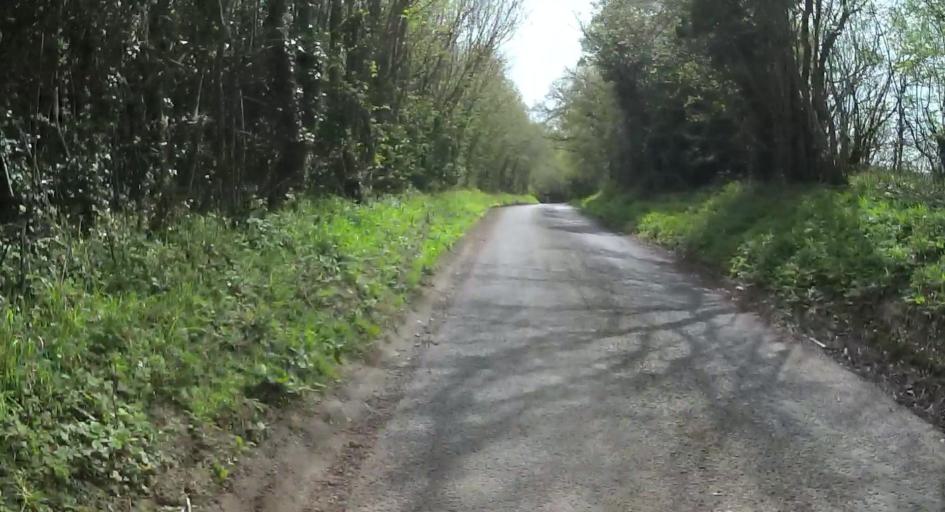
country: GB
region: England
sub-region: Hampshire
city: Alton
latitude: 51.1738
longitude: -0.9612
